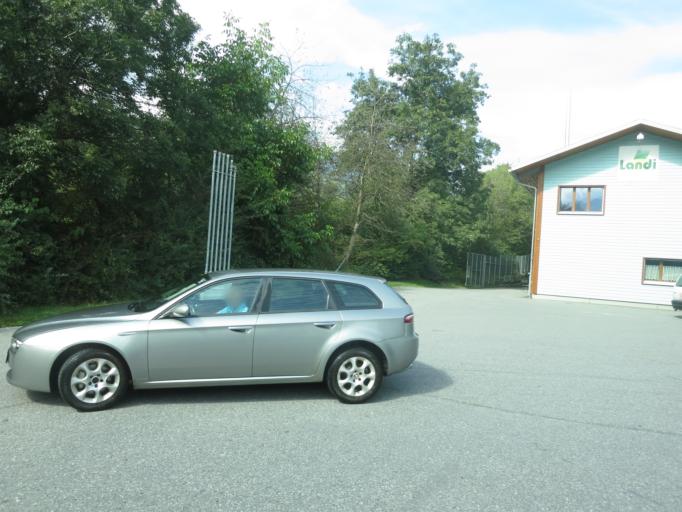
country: CH
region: Grisons
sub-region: Hinterrhein District
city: Cazis
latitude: 46.7109
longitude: 9.4353
